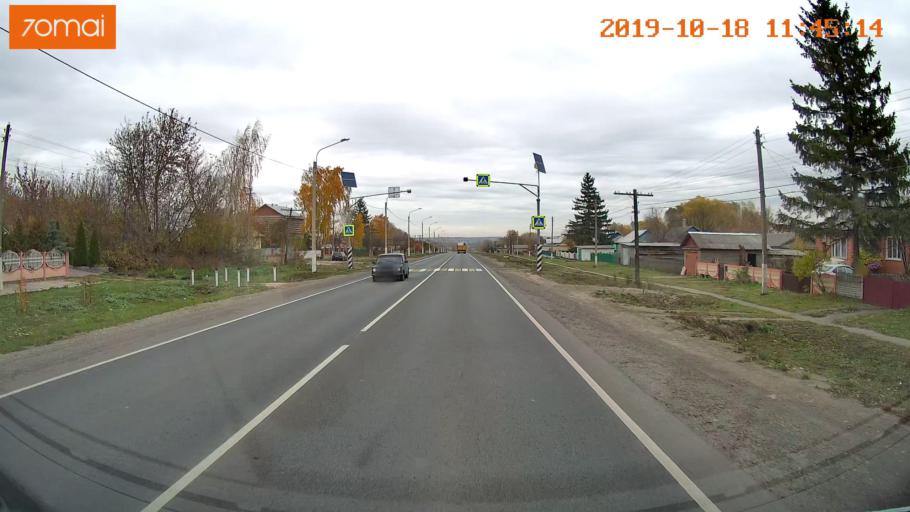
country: RU
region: Rjazan
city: Mikhaylov
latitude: 54.2089
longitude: 38.9677
